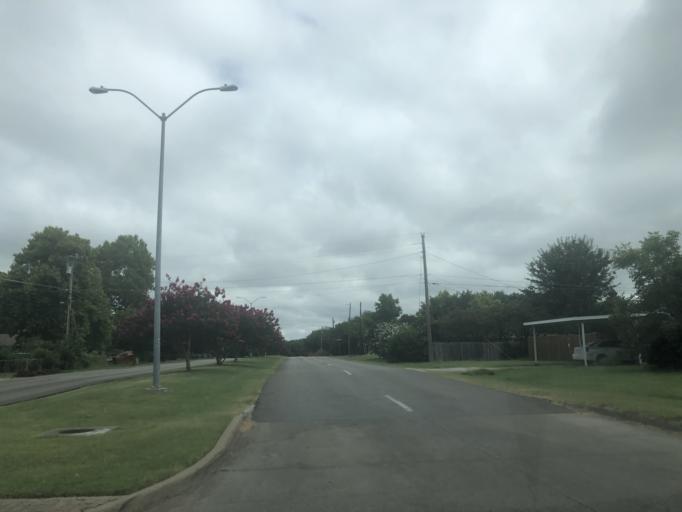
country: US
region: Texas
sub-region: Dallas County
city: Duncanville
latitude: 32.6619
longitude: -96.9170
